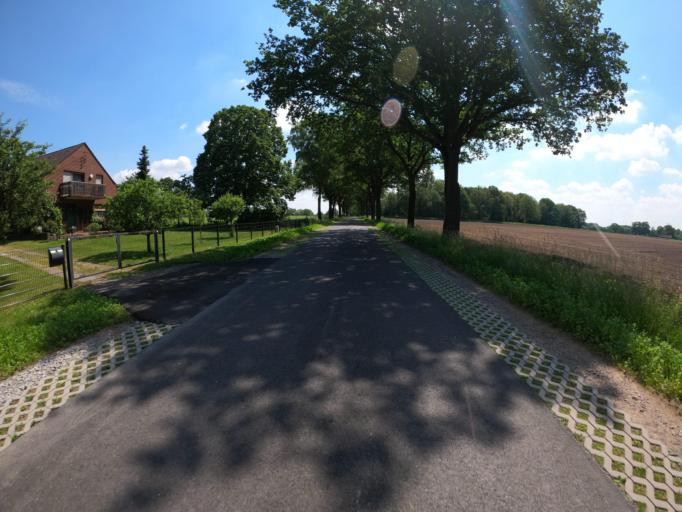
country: DE
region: North Rhine-Westphalia
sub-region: Regierungsbezirk Dusseldorf
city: Hunxe
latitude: 51.6979
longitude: 6.8065
